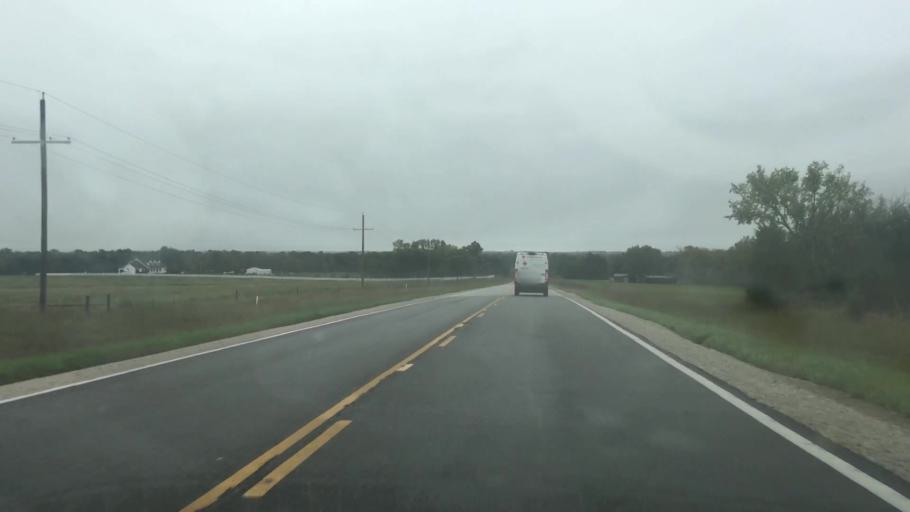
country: US
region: Kansas
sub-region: Anderson County
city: Garnett
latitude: 38.2237
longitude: -95.2485
